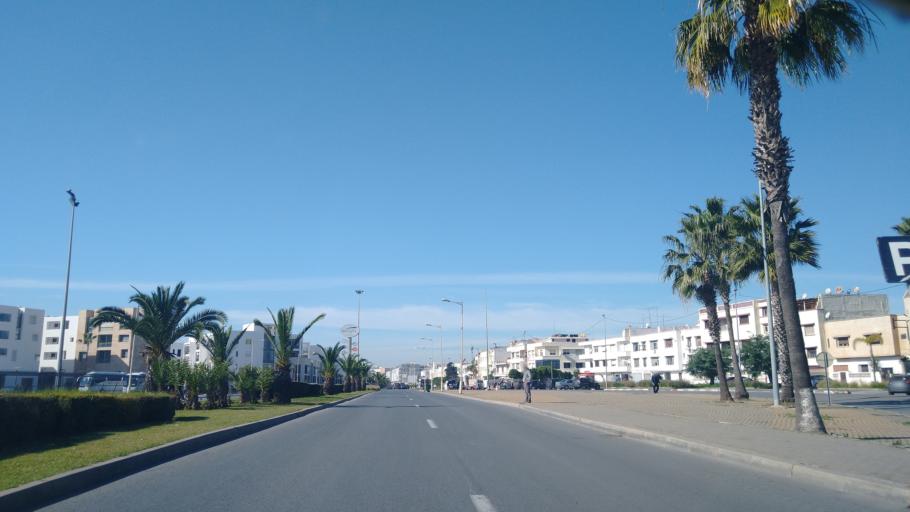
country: MA
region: Rabat-Sale-Zemmour-Zaer
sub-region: Rabat
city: Rabat
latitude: 34.0318
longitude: -6.8207
